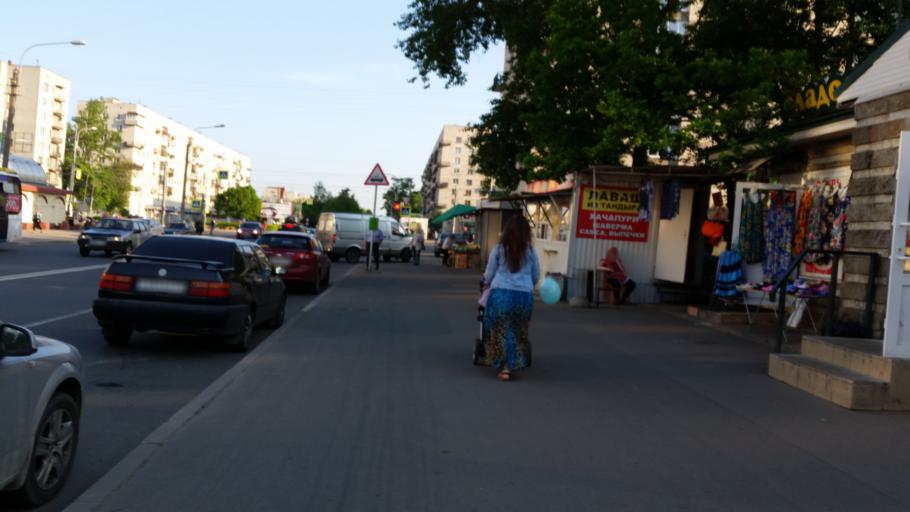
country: RU
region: St.-Petersburg
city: Sosnovaya Polyana
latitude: 59.8364
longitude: 30.1465
